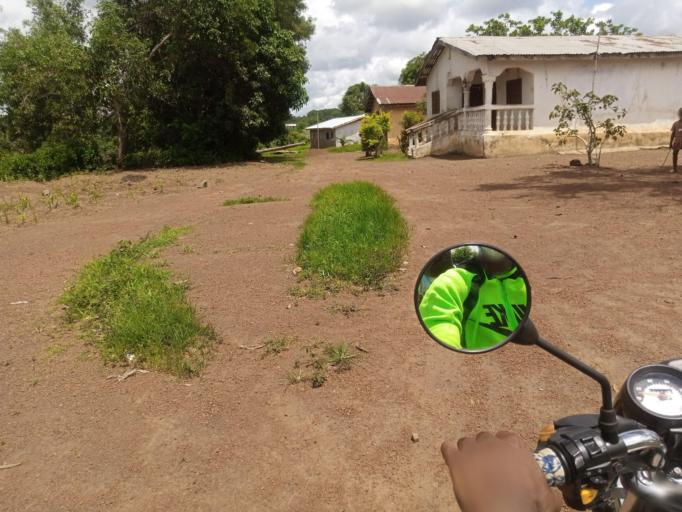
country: SL
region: Northern Province
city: Port Loko
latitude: 8.7580
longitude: -12.7819
